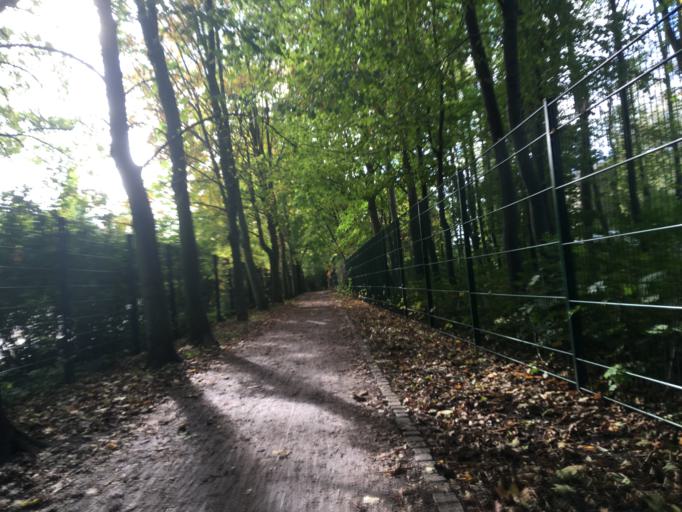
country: DE
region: Berlin
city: Mariendorf
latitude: 52.4340
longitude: 13.4081
